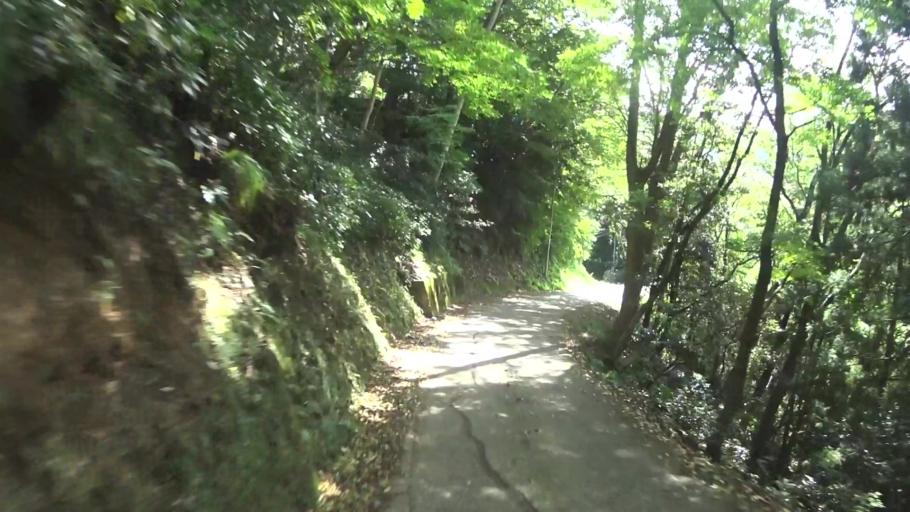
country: JP
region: Kyoto
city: Miyazu
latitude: 35.7413
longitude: 135.1865
